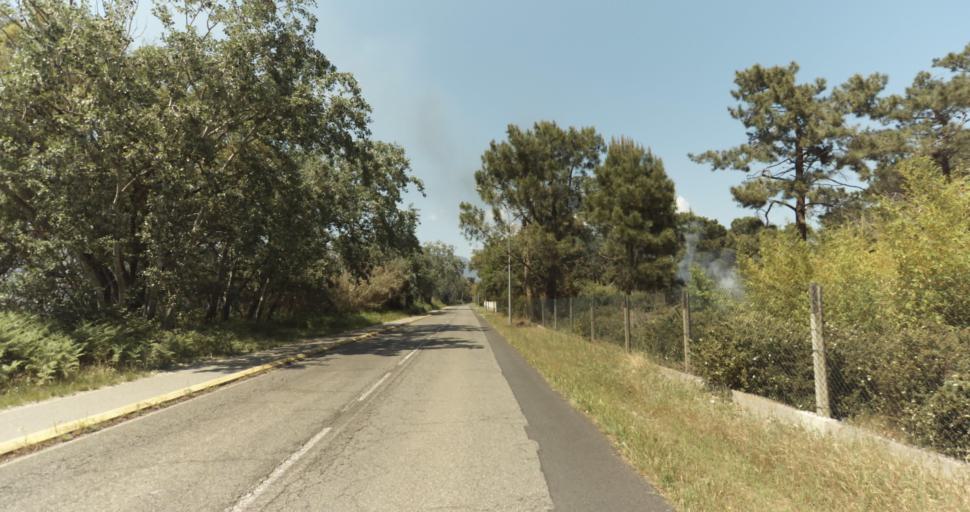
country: FR
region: Corsica
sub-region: Departement de la Haute-Corse
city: Biguglia
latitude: 42.6314
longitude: 9.4651
